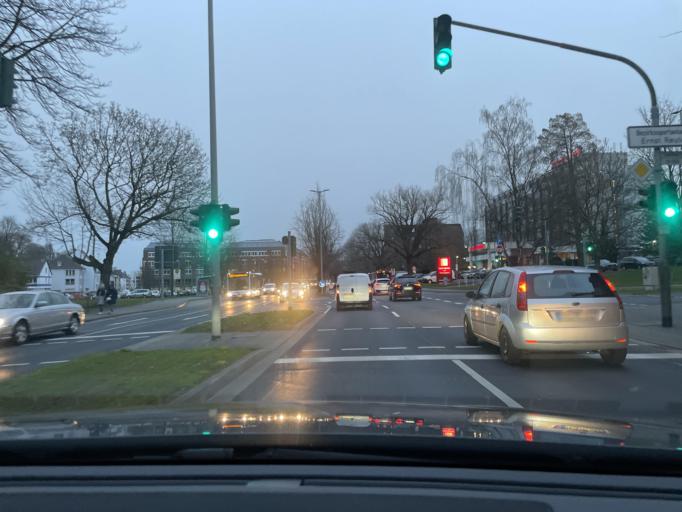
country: DE
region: North Rhine-Westphalia
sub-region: Regierungsbezirk Dusseldorf
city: Monchengladbach
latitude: 51.1913
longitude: 6.4294
